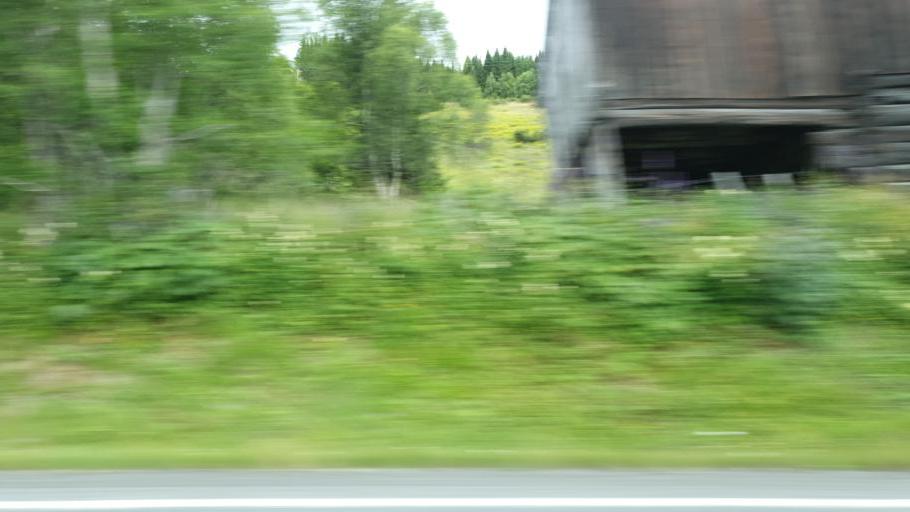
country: NO
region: Sor-Trondelag
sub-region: Rennebu
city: Berkak
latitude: 62.8693
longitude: 10.0315
